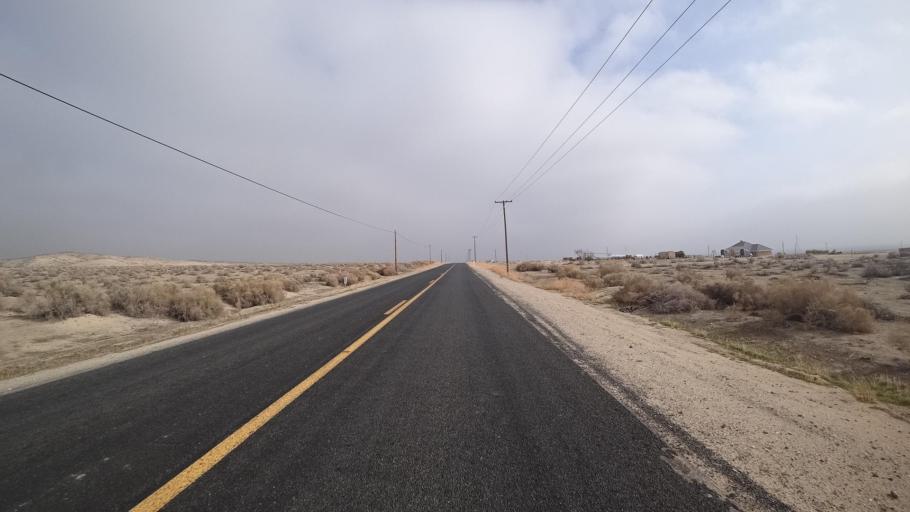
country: US
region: California
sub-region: Kern County
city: Ford City
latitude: 35.2326
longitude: -119.3619
